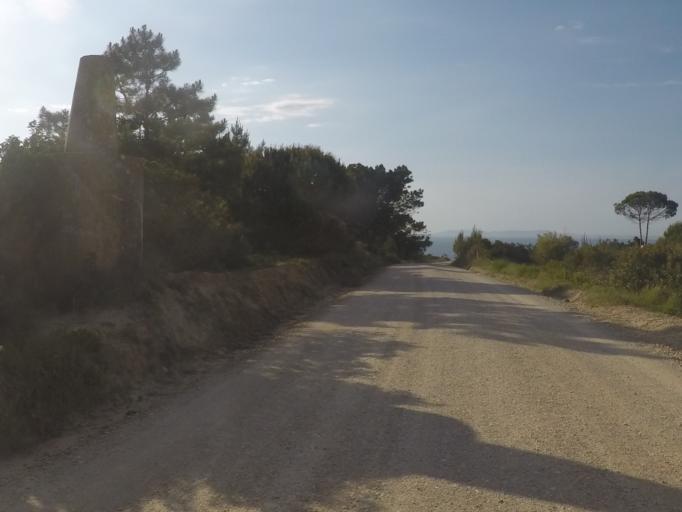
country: PT
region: Setubal
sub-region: Sesimbra
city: Sesimbra
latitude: 38.4475
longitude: -9.1992
